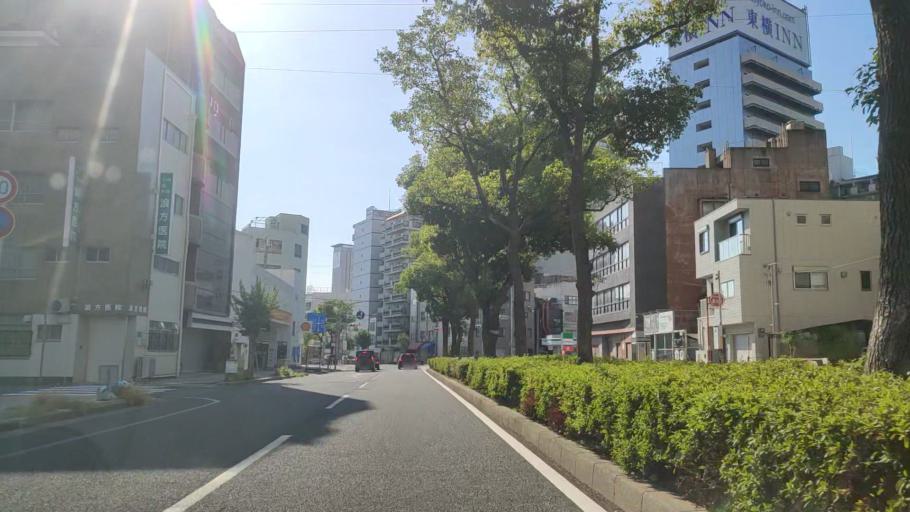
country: JP
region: Hyogo
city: Kobe
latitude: 34.6778
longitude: 135.1756
